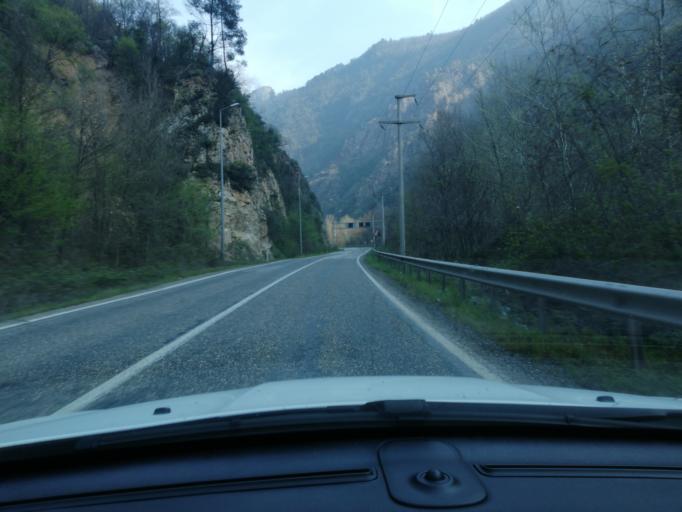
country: TR
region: Karabuk
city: Yenice
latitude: 41.1776
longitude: 32.4472
